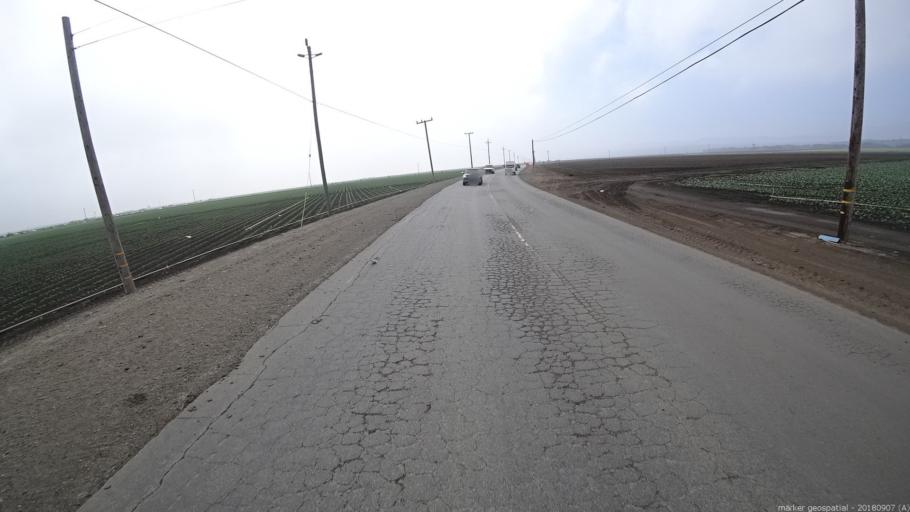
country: US
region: California
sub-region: Monterey County
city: Castroville
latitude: 36.7207
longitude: -121.7429
